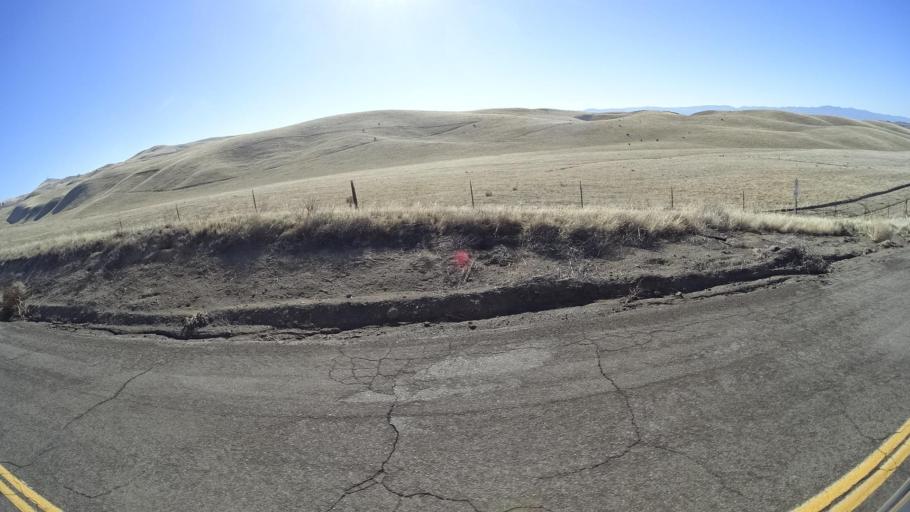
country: US
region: California
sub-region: Kern County
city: Maricopa
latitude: 34.9519
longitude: -119.4243
